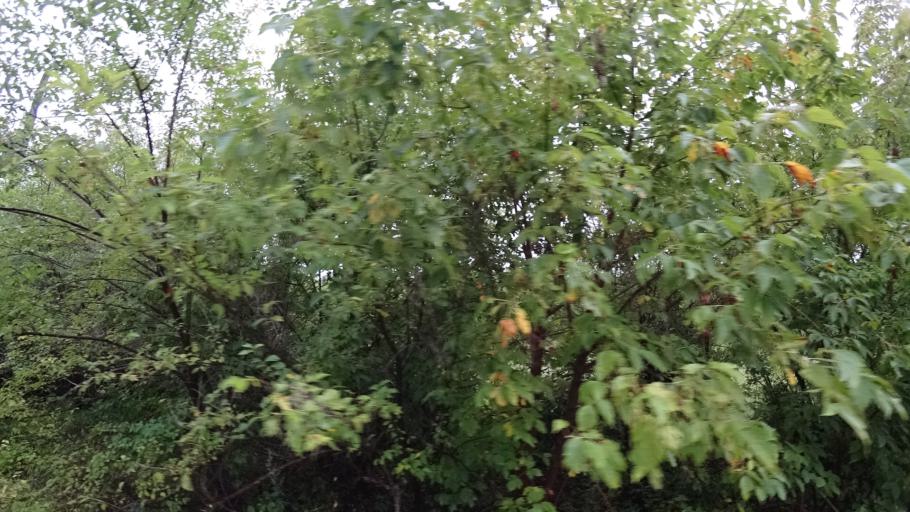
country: RU
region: Primorskiy
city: Monastyrishche
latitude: 44.2653
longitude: 132.4041
